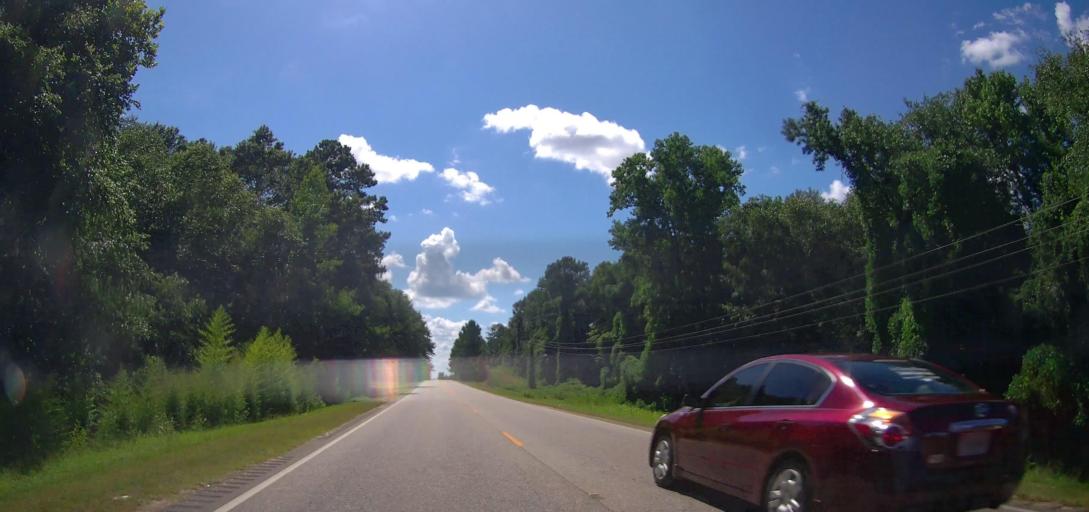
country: US
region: Alabama
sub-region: Elmore County
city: Tallassee
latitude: 32.3989
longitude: -85.9289
